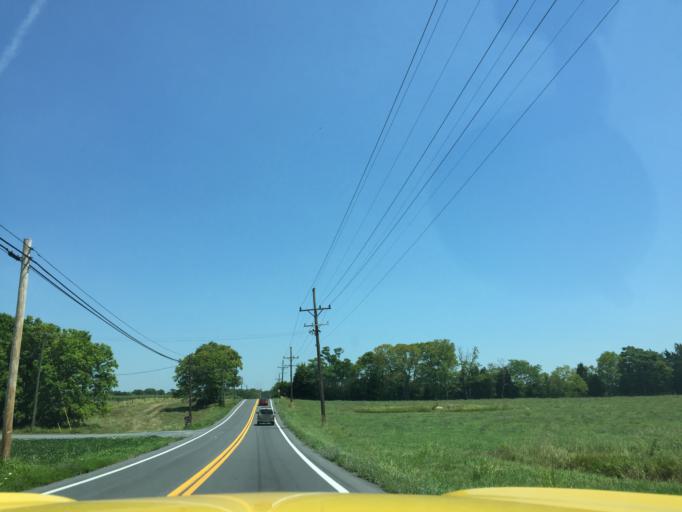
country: US
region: West Virginia
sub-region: Berkeley County
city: Inwood
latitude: 39.3045
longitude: -77.9628
